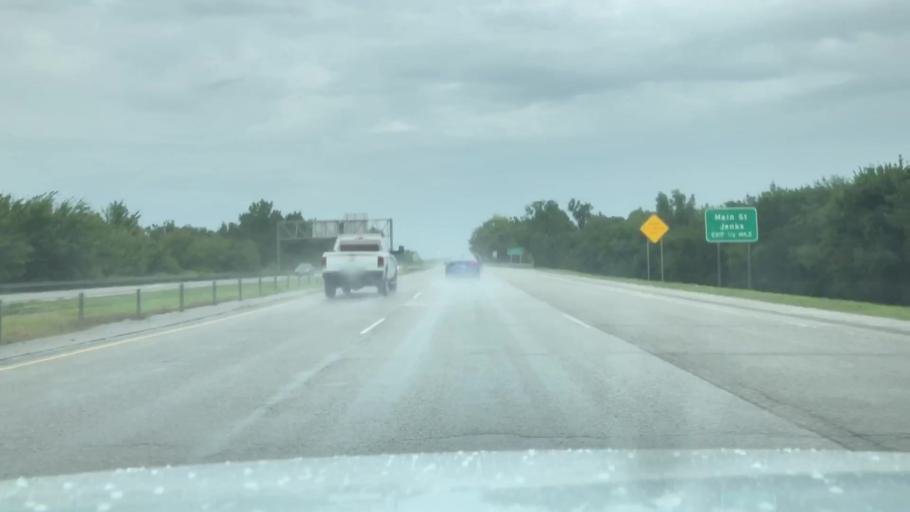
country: US
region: Oklahoma
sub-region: Tulsa County
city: Jenks
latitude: 36.0135
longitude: -96.0114
